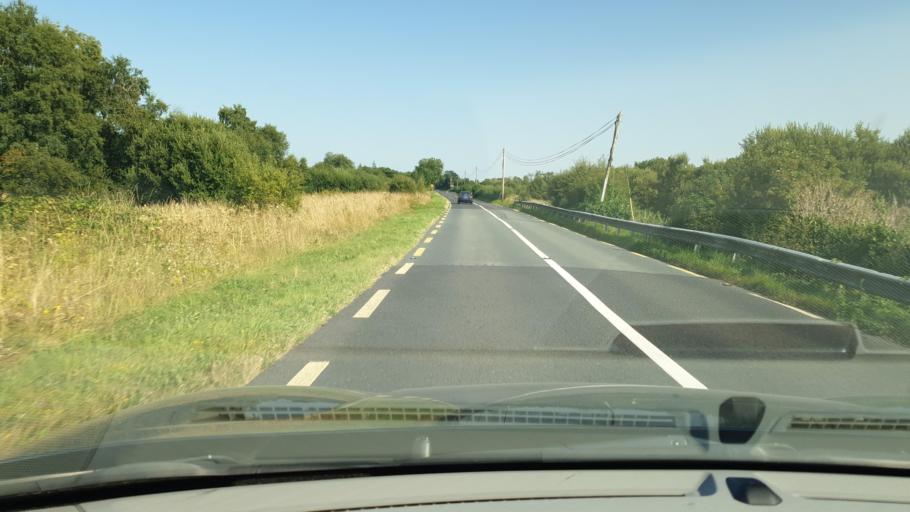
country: IE
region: Leinster
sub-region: An Mhi
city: Trim
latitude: 53.6344
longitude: -6.8162
